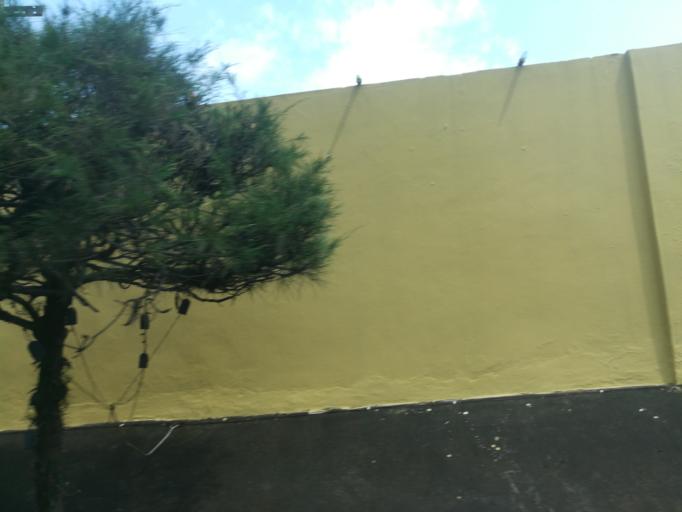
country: NG
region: Lagos
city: Ikeja
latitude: 6.6053
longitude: 3.3624
